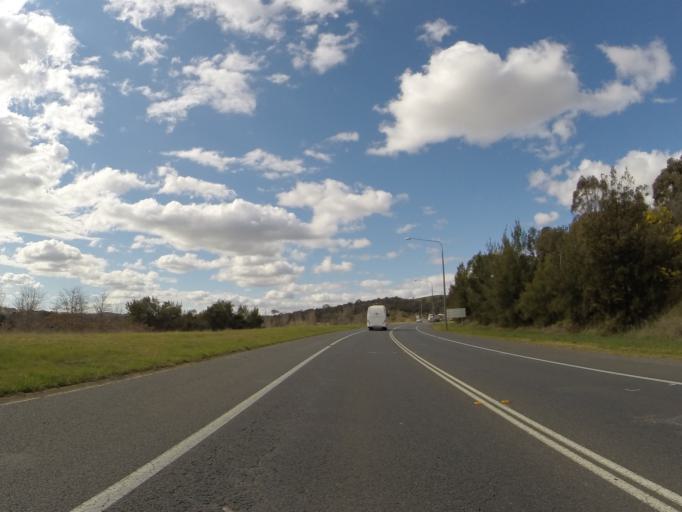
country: AU
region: Australian Capital Territory
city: Belconnen
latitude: -35.2038
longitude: 149.0903
